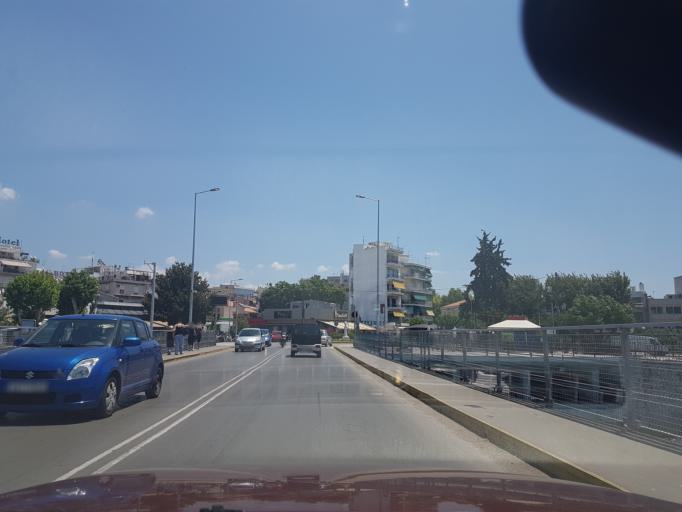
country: GR
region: Central Greece
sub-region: Nomos Evvoias
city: Chalkida
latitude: 38.4629
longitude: 23.5892
